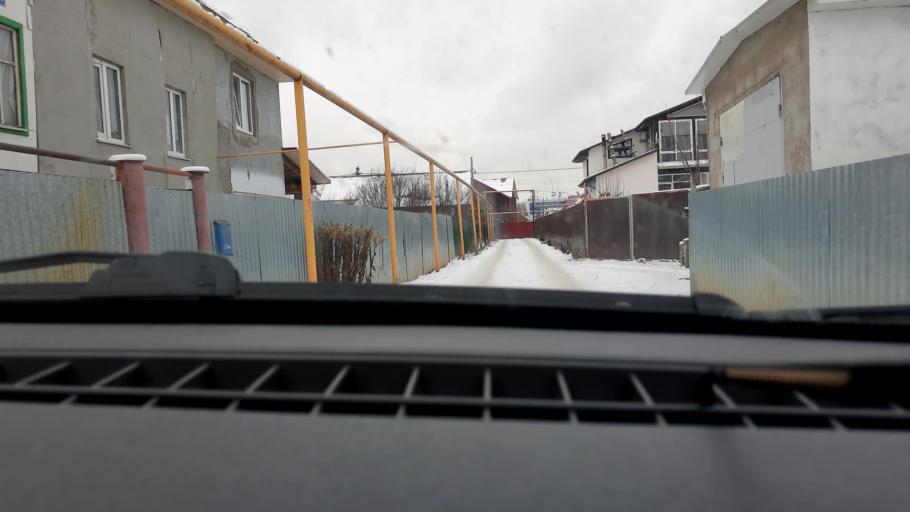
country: RU
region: Bashkortostan
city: Ufa
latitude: 54.6997
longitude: 55.9574
